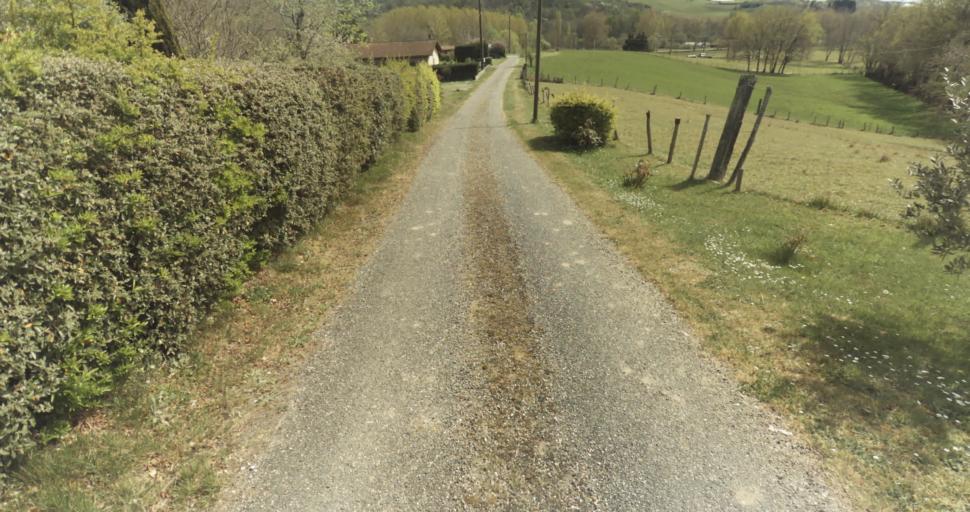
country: FR
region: Midi-Pyrenees
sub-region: Departement du Tarn-et-Garonne
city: Moissac
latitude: 44.1513
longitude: 1.1044
